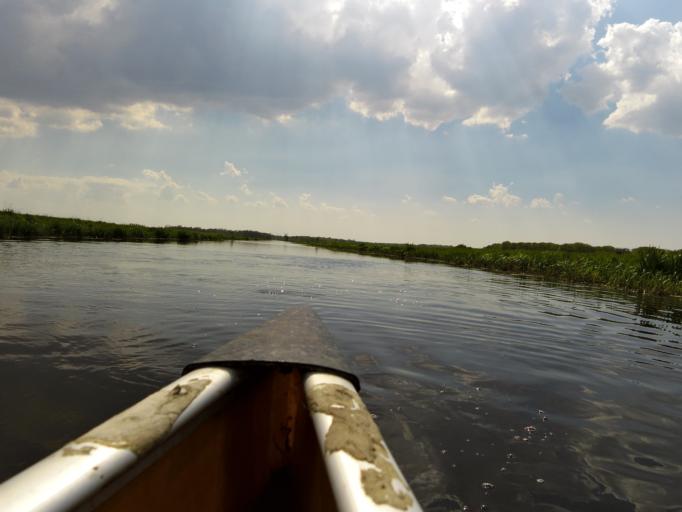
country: NL
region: South Holland
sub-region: Gemeente Voorschoten
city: Voorschoten
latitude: 52.1462
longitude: 4.4371
